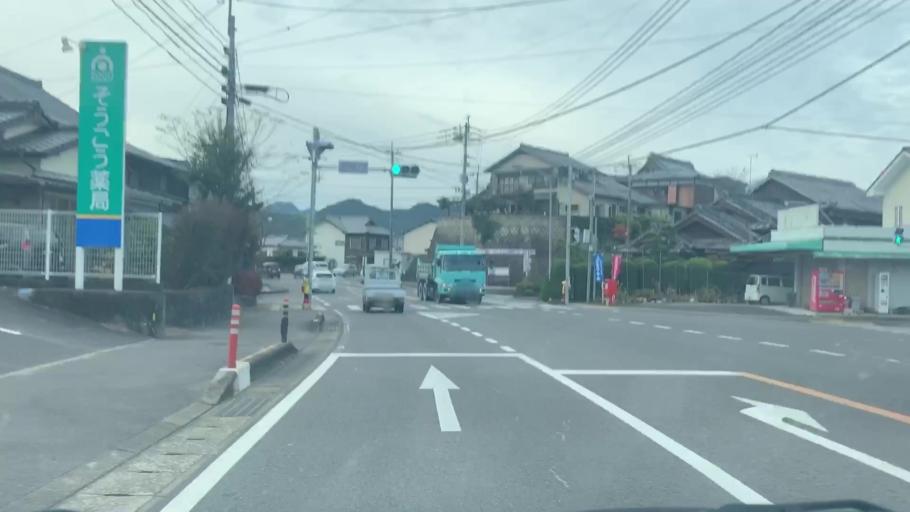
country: JP
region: Saga Prefecture
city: Kashima
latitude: 33.1325
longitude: 130.0615
